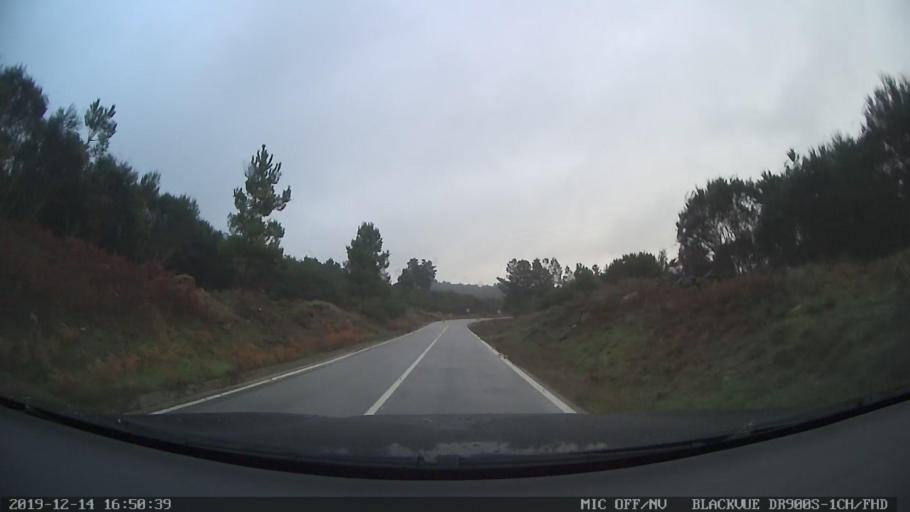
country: PT
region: Vila Real
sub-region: Murca
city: Murca
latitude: 41.4177
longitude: -7.5062
